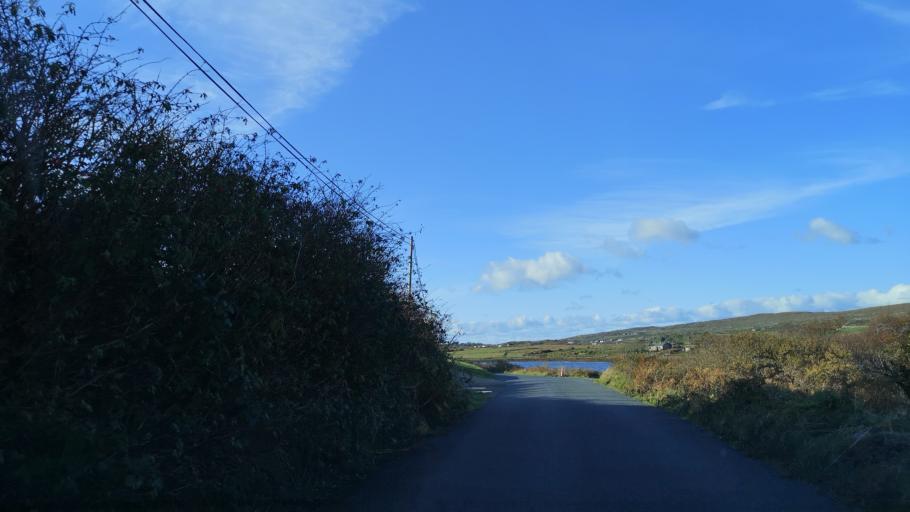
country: IE
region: Connaught
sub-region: County Galway
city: Clifden
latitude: 53.5053
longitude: -10.0732
